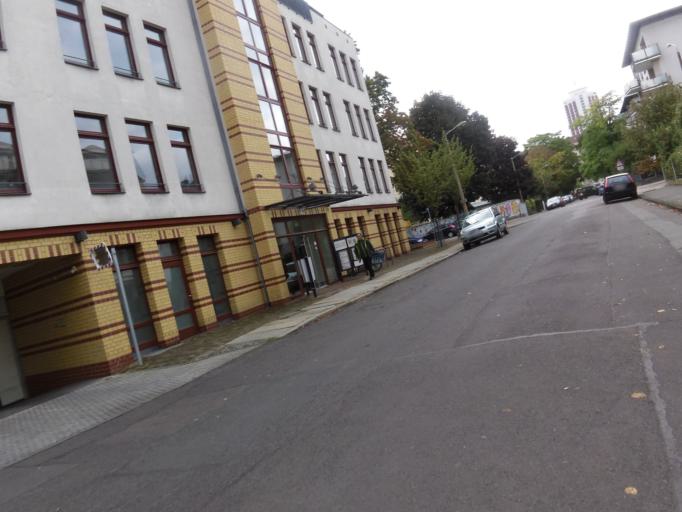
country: DE
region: Saxony
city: Leipzig
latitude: 51.3423
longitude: 12.3915
